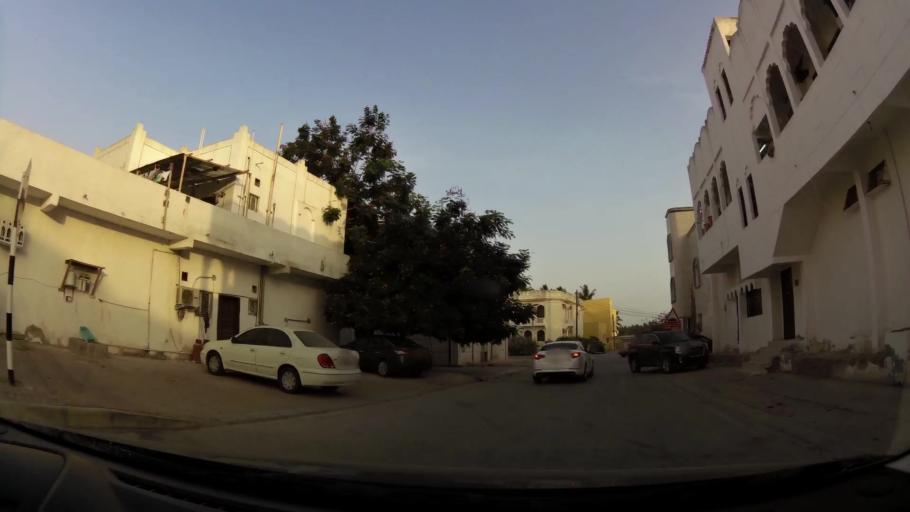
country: OM
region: Zufar
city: Salalah
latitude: 17.0156
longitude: 54.1142
